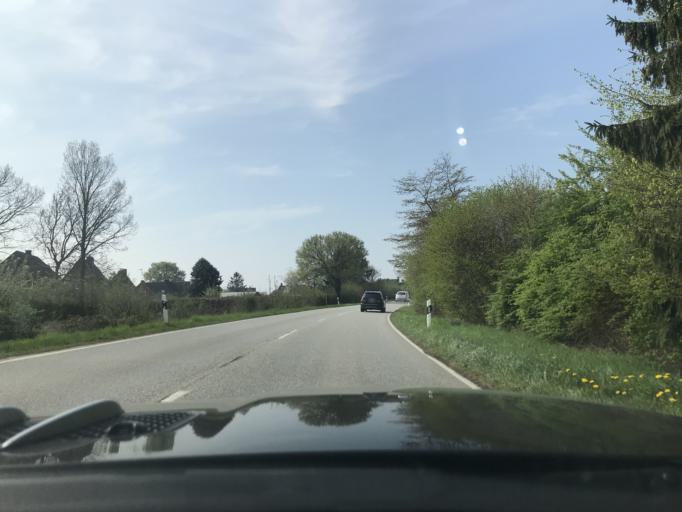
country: DE
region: Schleswig-Holstein
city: Gromitz
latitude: 54.1715
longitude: 10.9771
